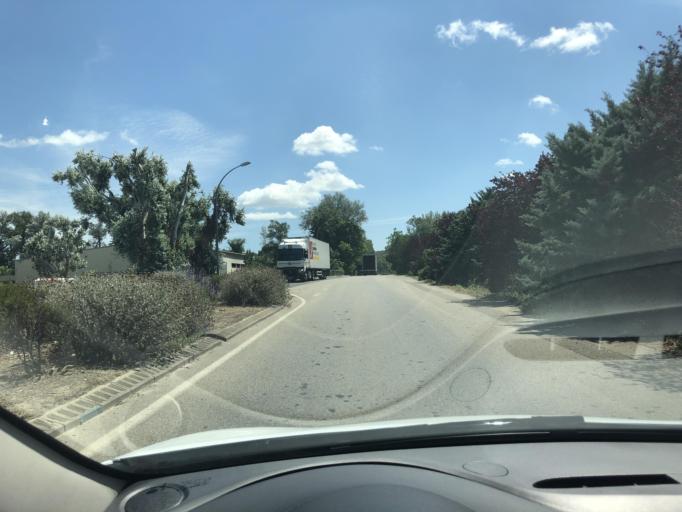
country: FR
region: Provence-Alpes-Cote d'Azur
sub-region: Departement des Bouches-du-Rhone
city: Noves
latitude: 43.8912
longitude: 4.8802
